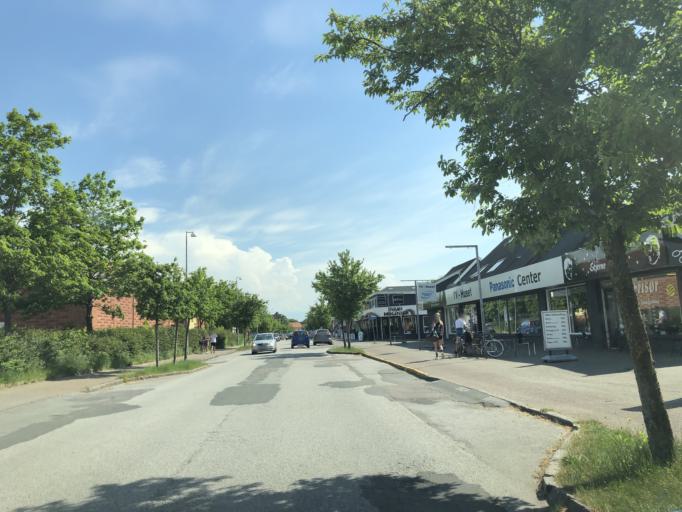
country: DK
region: Central Jutland
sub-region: Holstebro Kommune
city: Holstebro
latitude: 56.3675
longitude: 8.6177
